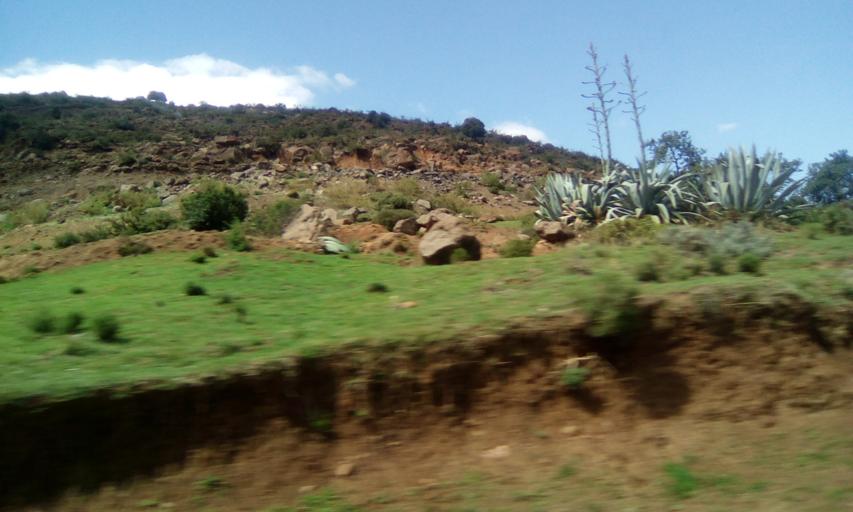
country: LS
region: Maseru
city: Nako
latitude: -29.6562
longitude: 27.8372
